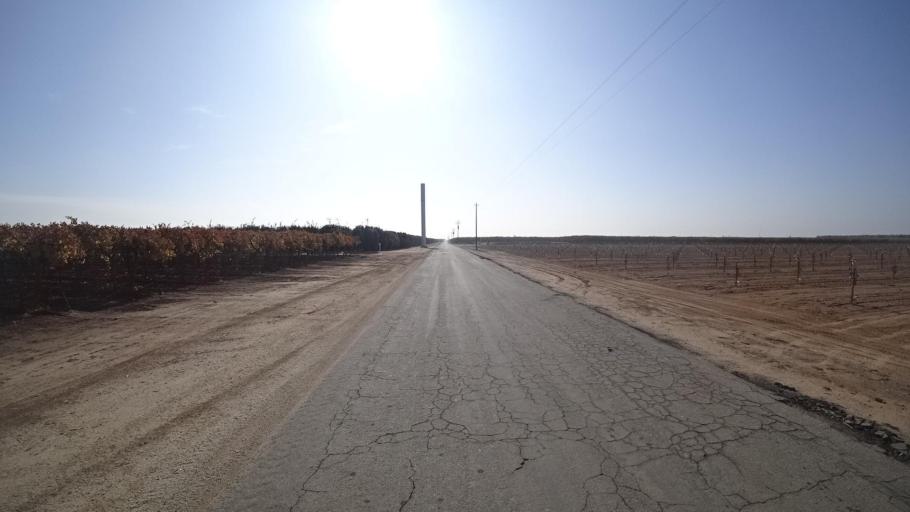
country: US
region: California
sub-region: Kern County
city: McFarland
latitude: 35.6222
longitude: -119.1865
